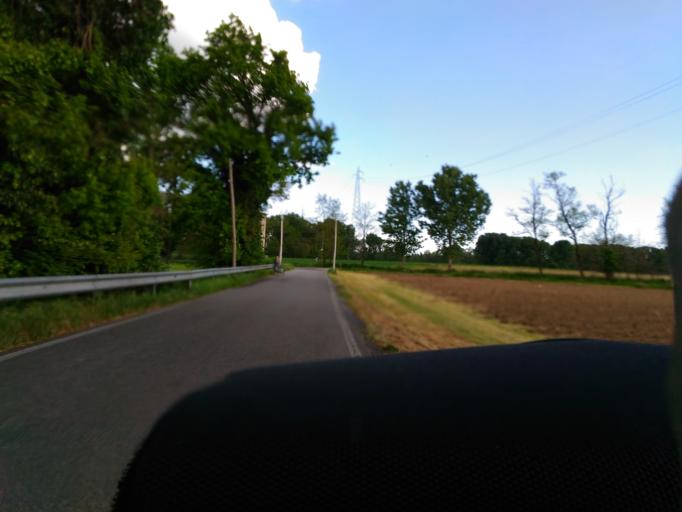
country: IT
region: Lombardy
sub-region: Citta metropolitana di Milano
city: Triginto
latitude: 45.4008
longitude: 9.3152
